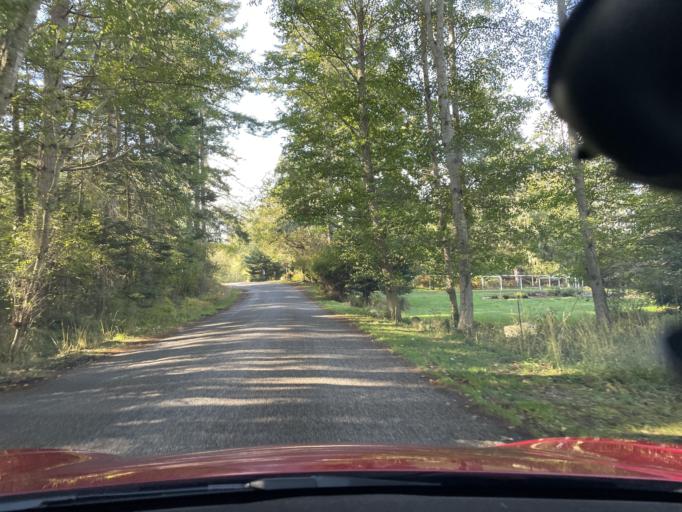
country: US
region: Washington
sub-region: San Juan County
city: Friday Harbor
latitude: 48.4595
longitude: -122.9650
